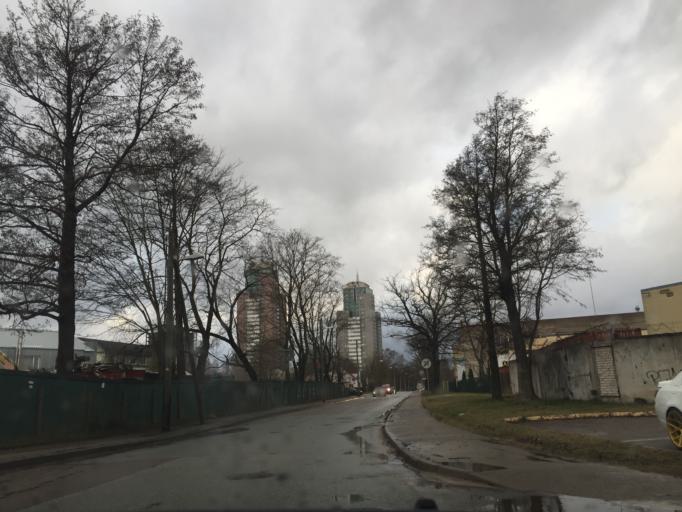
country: LV
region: Marupe
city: Marupe
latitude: 56.9319
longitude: 24.0502
